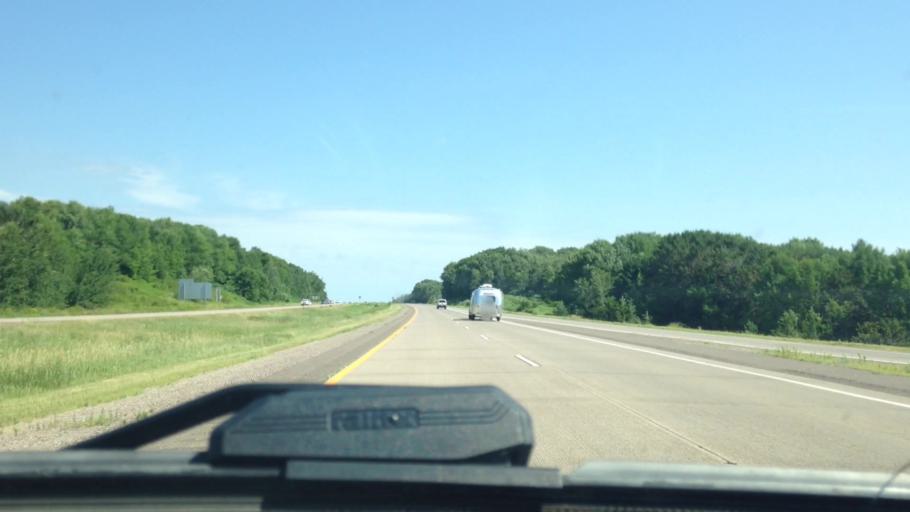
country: US
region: Wisconsin
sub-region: Barron County
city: Rice Lake
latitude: 45.5129
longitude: -91.7608
